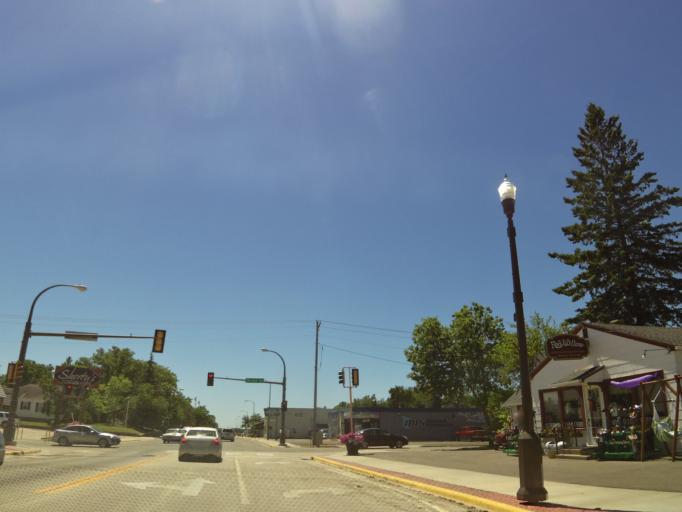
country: US
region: Minnesota
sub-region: Becker County
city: Detroit Lakes
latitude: 46.8117
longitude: -95.8457
